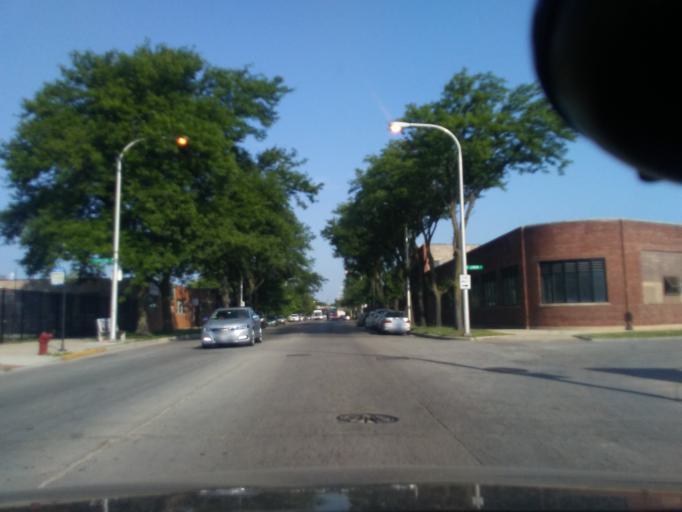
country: US
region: Illinois
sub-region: Cook County
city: Oak Park
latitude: 41.9152
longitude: -87.7493
